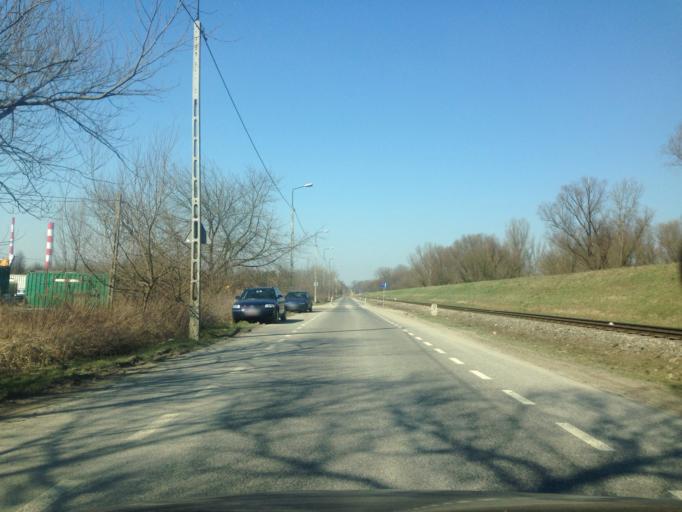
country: PL
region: Masovian Voivodeship
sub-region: Warszawa
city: Wilanow
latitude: 52.1772
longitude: 21.1163
